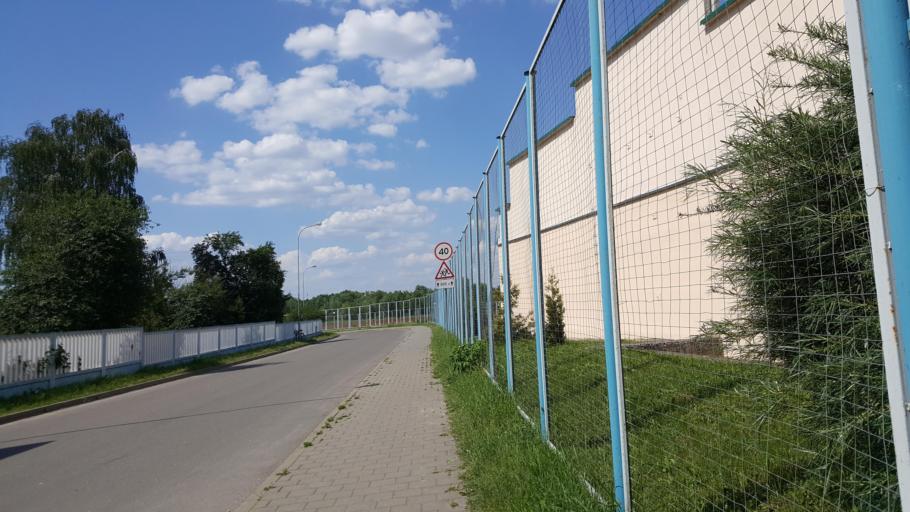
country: BY
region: Brest
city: Horad Kobryn
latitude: 52.2122
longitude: 24.3678
